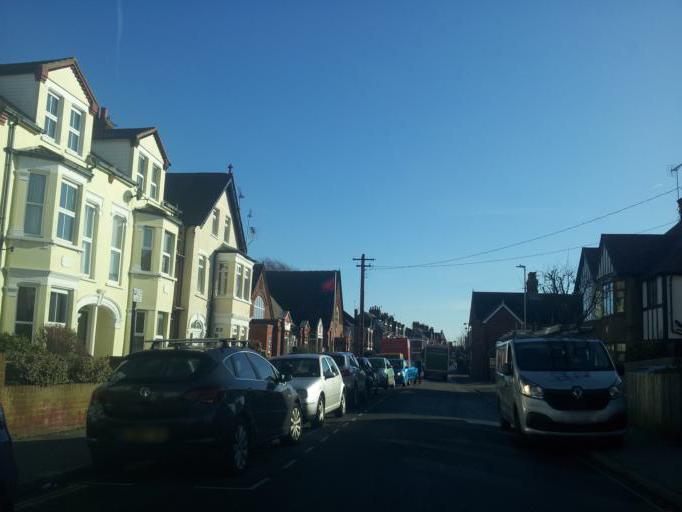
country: GB
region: England
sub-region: Suffolk
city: Felixstowe
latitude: 51.9636
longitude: 1.3526
